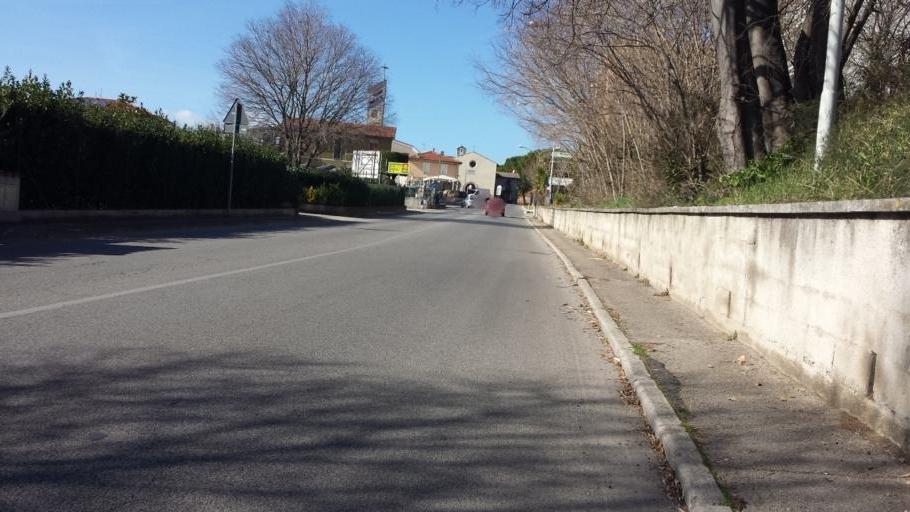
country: IT
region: Umbria
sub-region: Provincia di Terni
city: Terni
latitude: 42.5848
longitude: 12.6131
